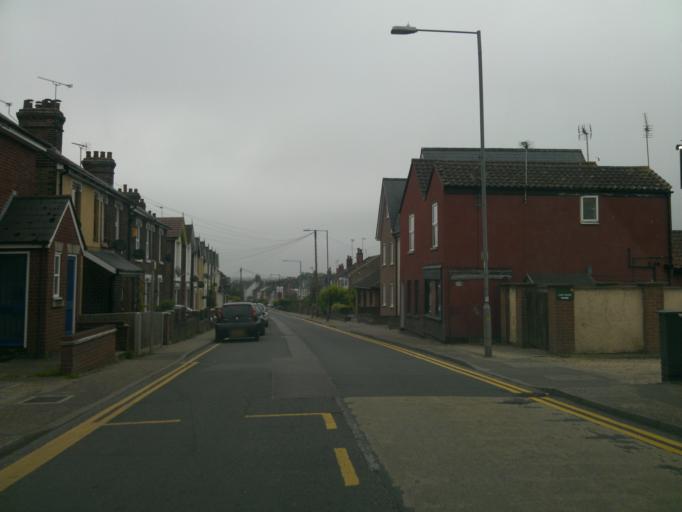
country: GB
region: England
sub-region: Essex
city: Colchester
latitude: 51.9044
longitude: 0.8873
